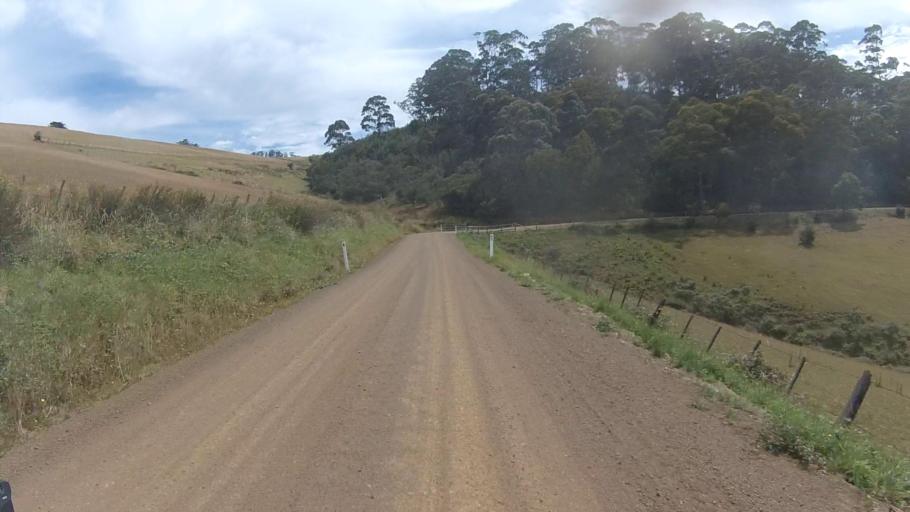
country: AU
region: Tasmania
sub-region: Sorell
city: Sorell
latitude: -42.7940
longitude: 147.8418
